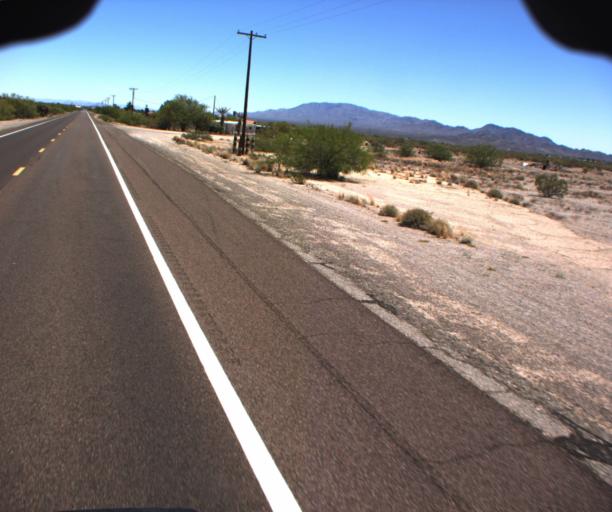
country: US
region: Arizona
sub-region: La Paz County
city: Salome
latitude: 33.7680
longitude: -113.6394
